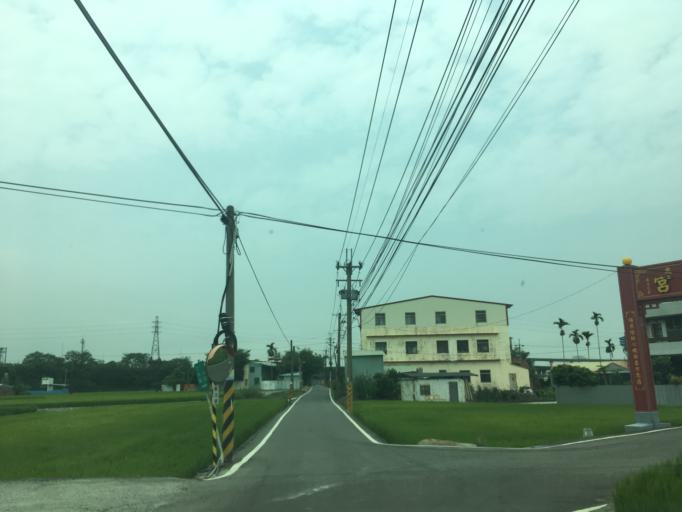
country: TW
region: Taiwan
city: Zhongxing New Village
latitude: 24.0414
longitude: 120.6813
